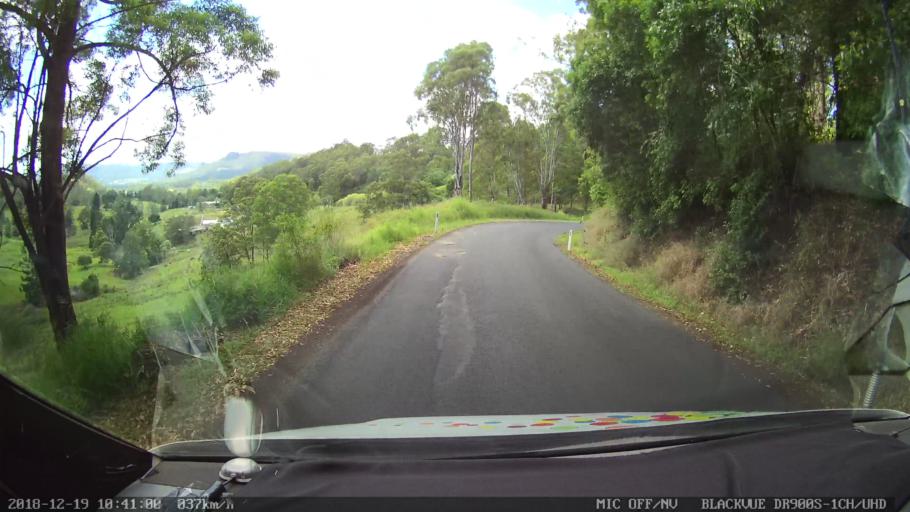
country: AU
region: New South Wales
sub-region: Lismore Municipality
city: Nimbin
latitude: -28.5875
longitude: 153.1601
